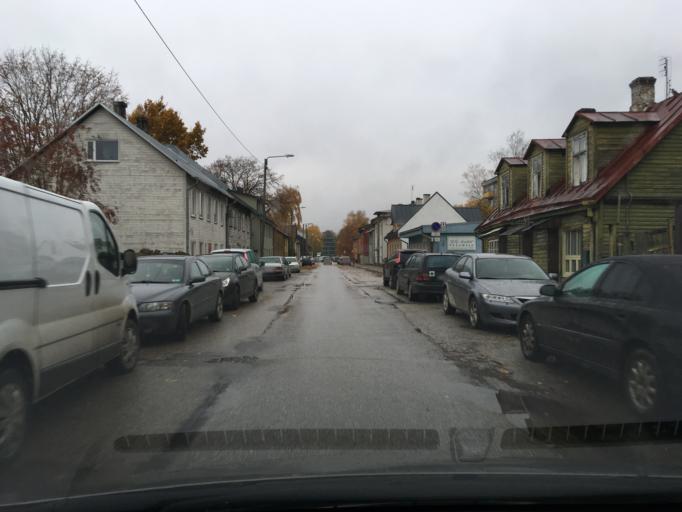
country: EE
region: Tartu
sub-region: Tartu linn
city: Tartu
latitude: 58.3806
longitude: 26.7421
